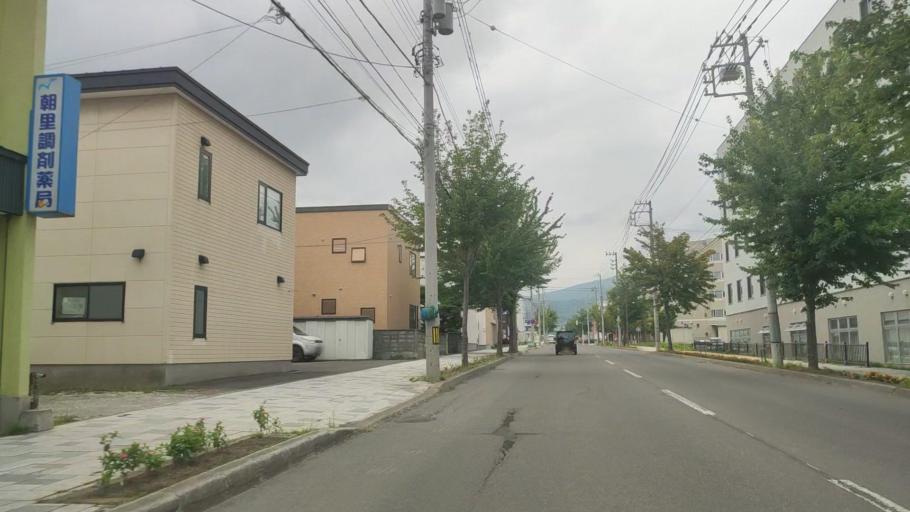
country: JP
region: Hokkaido
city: Otaru
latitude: 43.1731
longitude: 141.0554
